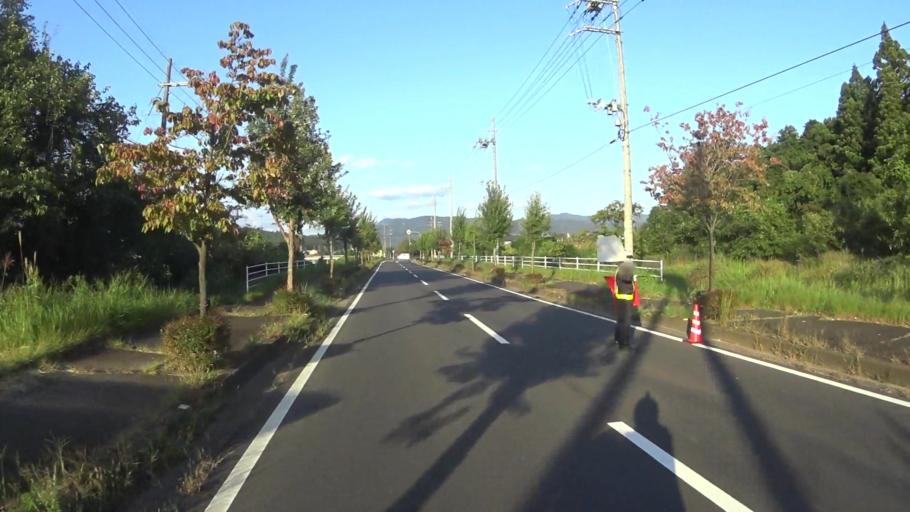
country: JP
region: Kyoto
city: Miyazu
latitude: 35.6048
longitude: 135.0527
